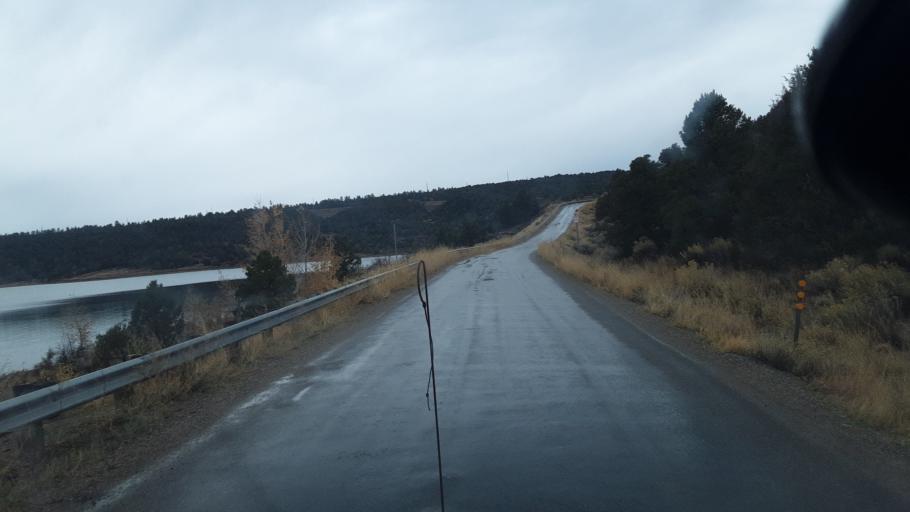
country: US
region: Colorado
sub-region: La Plata County
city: Durango
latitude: 37.2339
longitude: -107.9063
